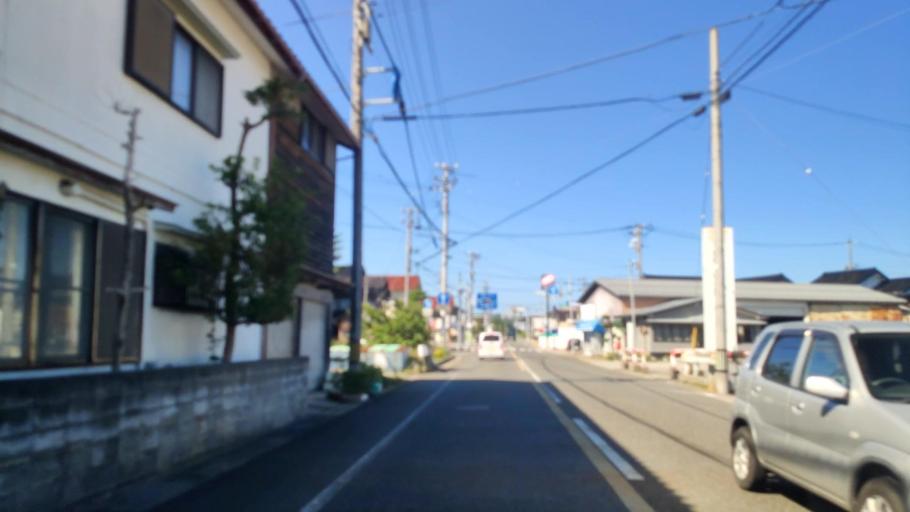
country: JP
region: Ishikawa
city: Nanao
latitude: 37.4427
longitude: 137.2646
